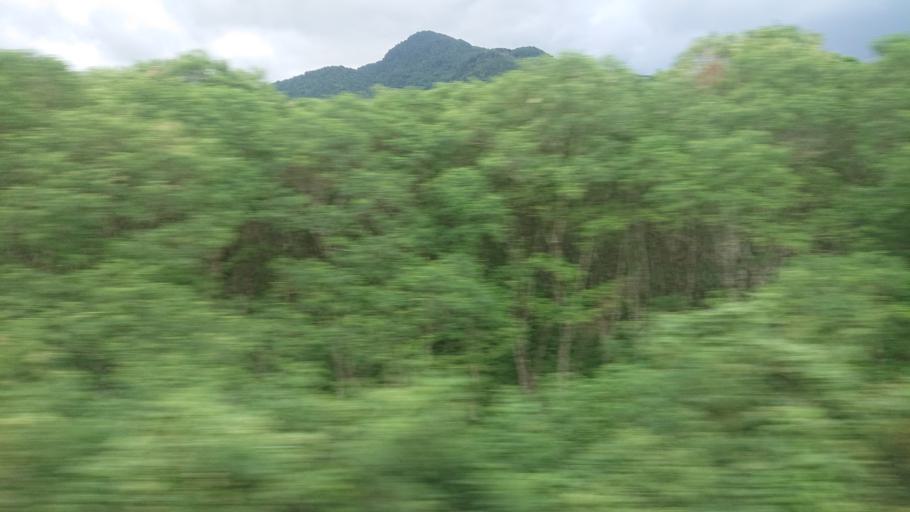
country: TW
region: Taiwan
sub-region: Hualien
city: Hualian
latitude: 23.6184
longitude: 121.3947
